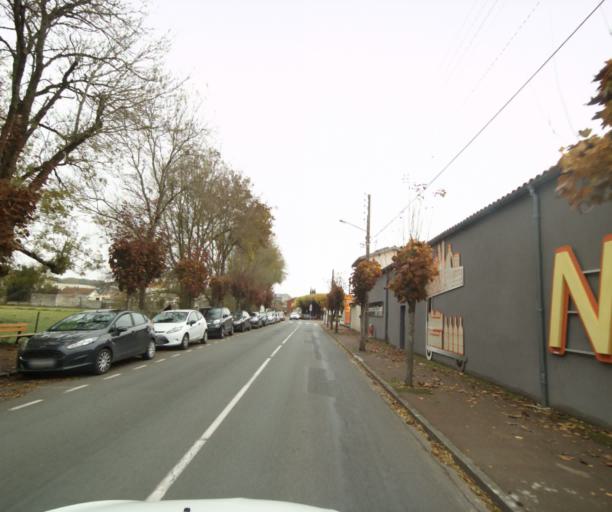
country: FR
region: Poitou-Charentes
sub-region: Departement de la Charente-Maritime
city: Saintes
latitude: 45.7482
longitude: -0.6235
